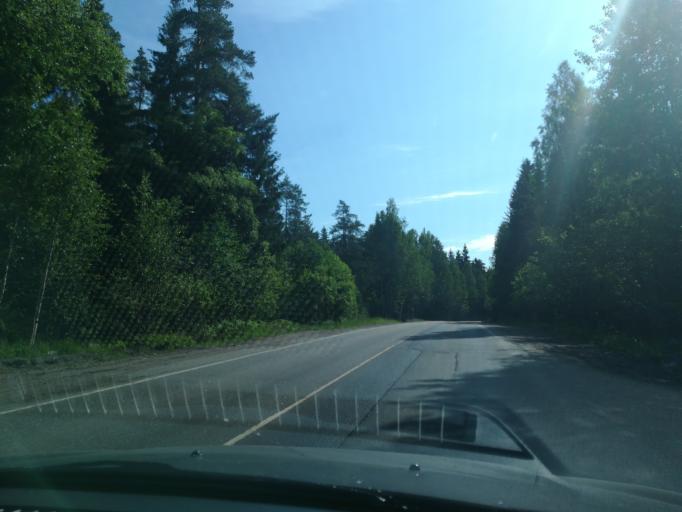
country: RU
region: Leningrad
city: Lesogorskiy
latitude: 60.9012
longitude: 28.8520
